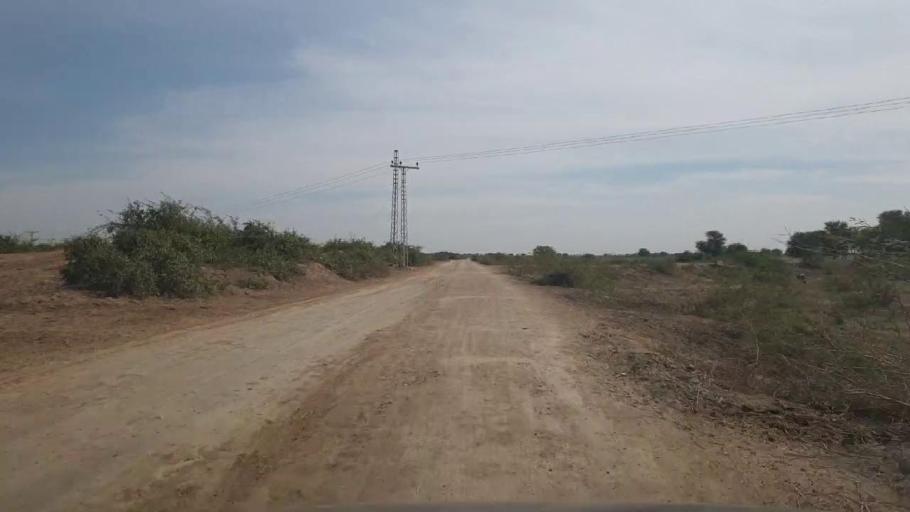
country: PK
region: Sindh
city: Kunri
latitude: 25.2948
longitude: 69.5820
